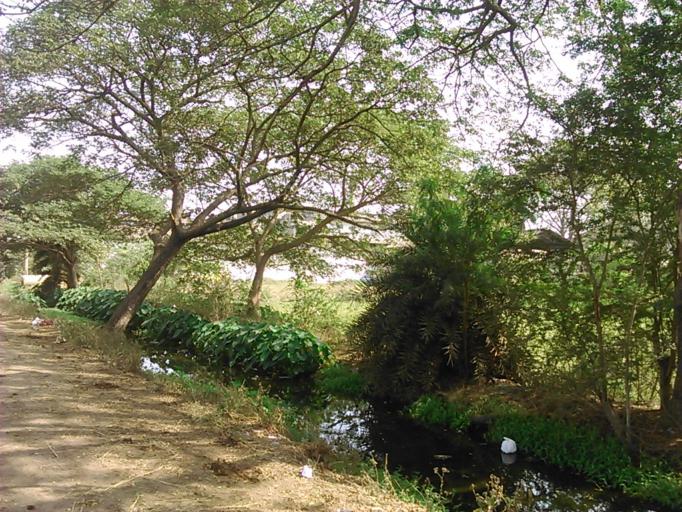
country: IN
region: Andhra Pradesh
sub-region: Guntur
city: Bhattiprolu
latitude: 16.2375
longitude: 80.6660
